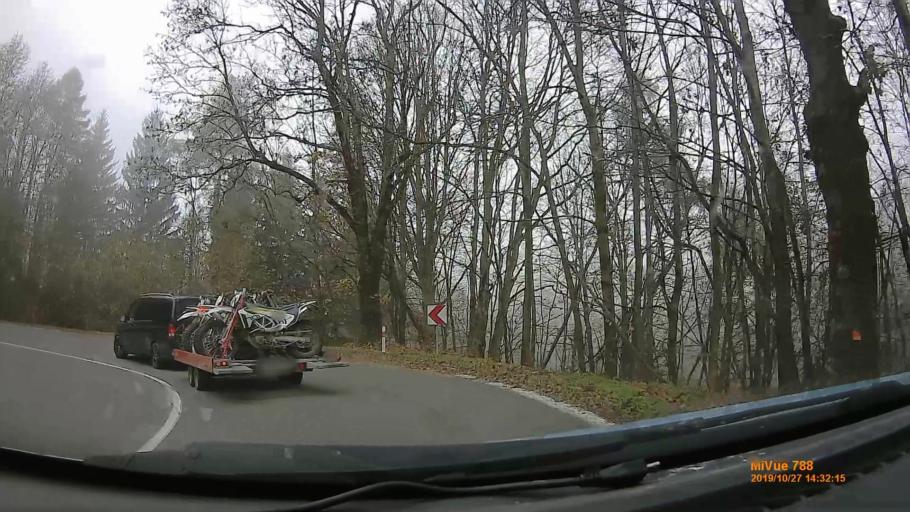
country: CZ
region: Olomoucky
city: Olsany
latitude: 49.9865
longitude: 16.8140
